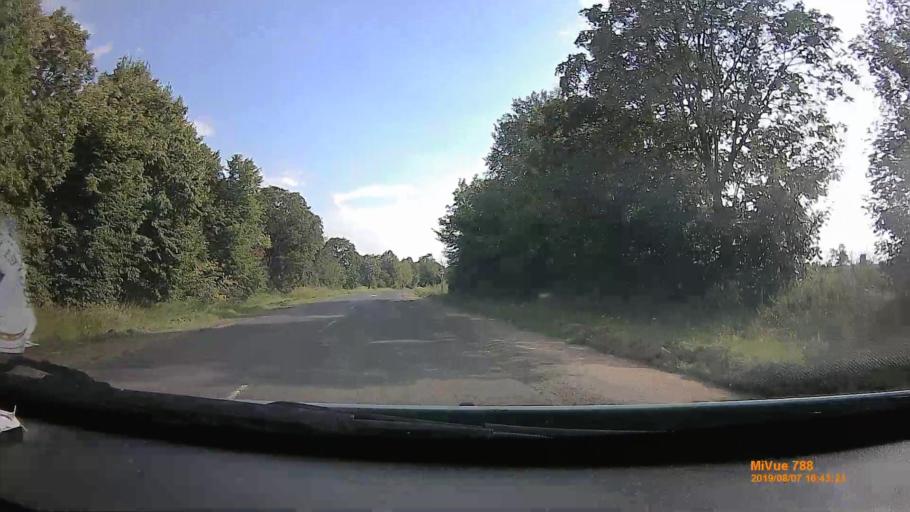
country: HU
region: Borsod-Abauj-Zemplen
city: Abaujszanto
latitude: 48.3574
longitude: 21.2152
